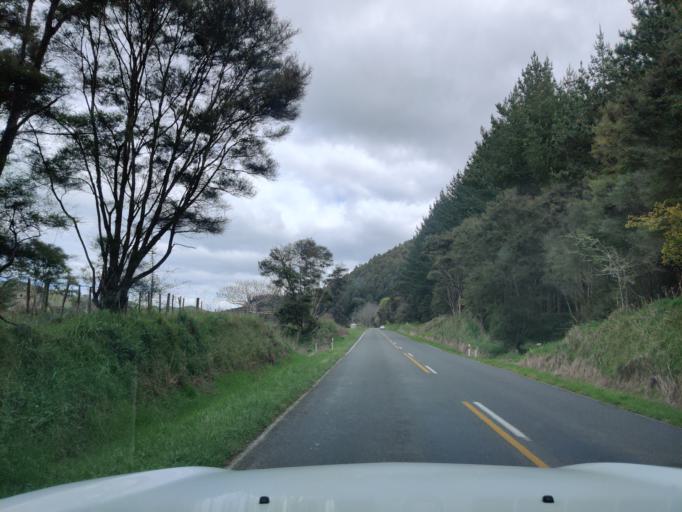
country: NZ
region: Manawatu-Wanganui
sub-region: Wanganui District
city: Wanganui
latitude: -39.8339
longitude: 175.1631
